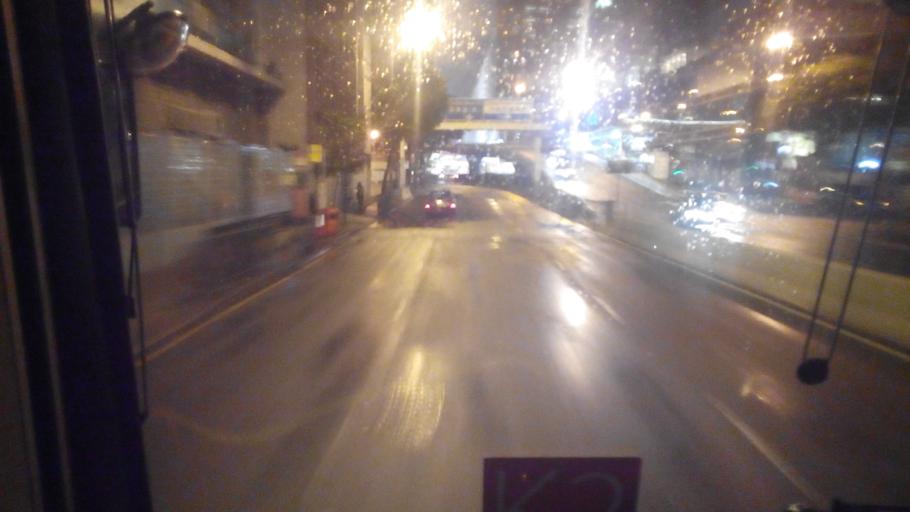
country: HK
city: Hong Kong
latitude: 22.3021
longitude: 114.1685
